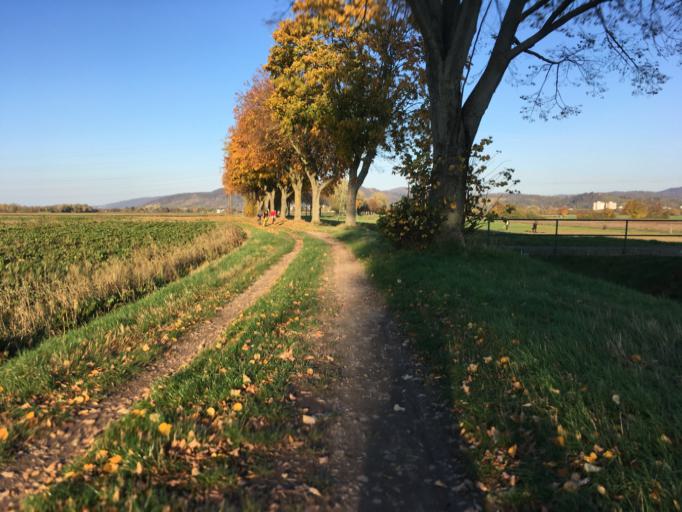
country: DE
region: Hesse
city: Lorsch
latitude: 49.6754
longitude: 8.5757
